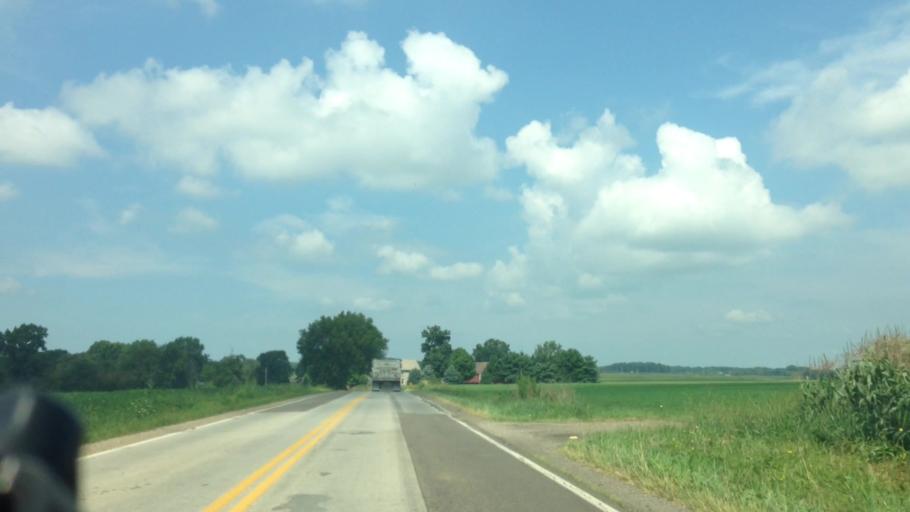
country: US
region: Ohio
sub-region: Wayne County
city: Orrville
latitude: 40.8742
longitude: -81.7104
